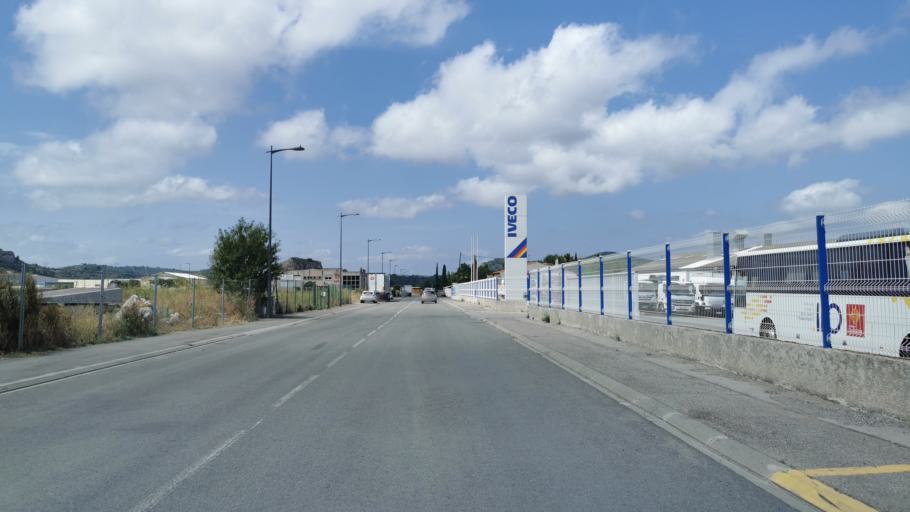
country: FR
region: Languedoc-Roussillon
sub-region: Departement de l'Aude
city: Marcorignan
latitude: 43.1818
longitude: 2.9411
